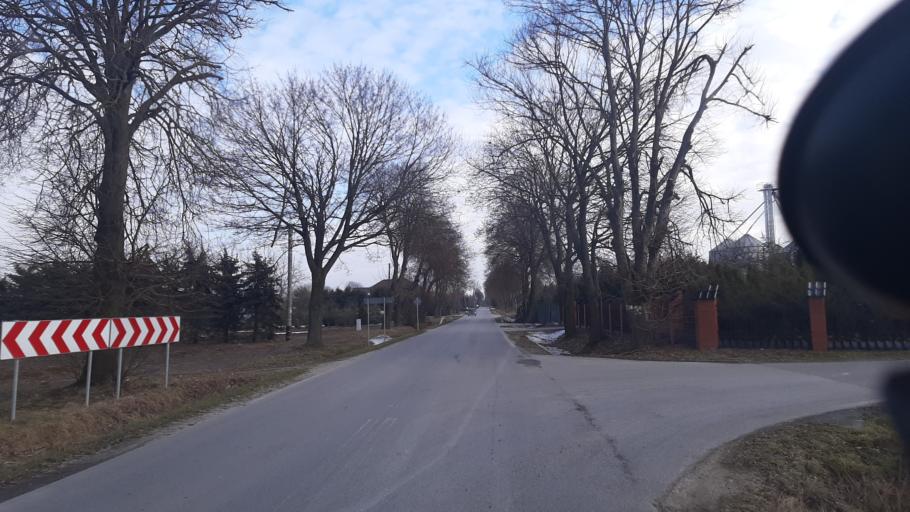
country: PL
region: Lublin Voivodeship
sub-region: Powiat lubartowski
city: Uscimow Stary
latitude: 51.4804
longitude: 22.9091
